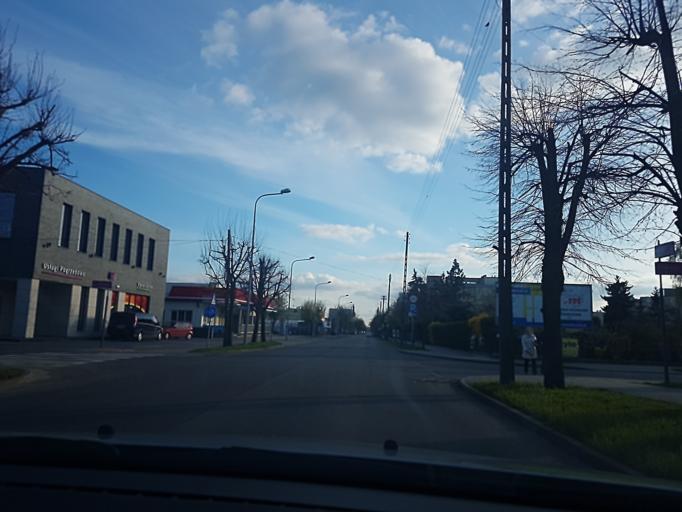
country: PL
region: Lodz Voivodeship
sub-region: Powiat kutnowski
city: Kutno
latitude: 52.2379
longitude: 19.3692
